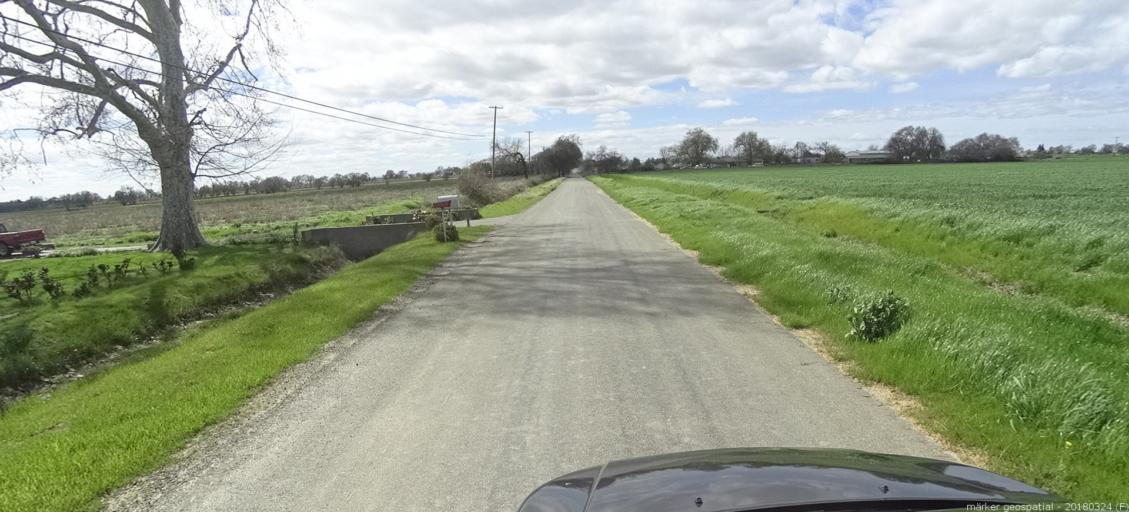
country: US
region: California
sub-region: Yolo County
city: West Sacramento
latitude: 38.6854
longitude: -121.6155
